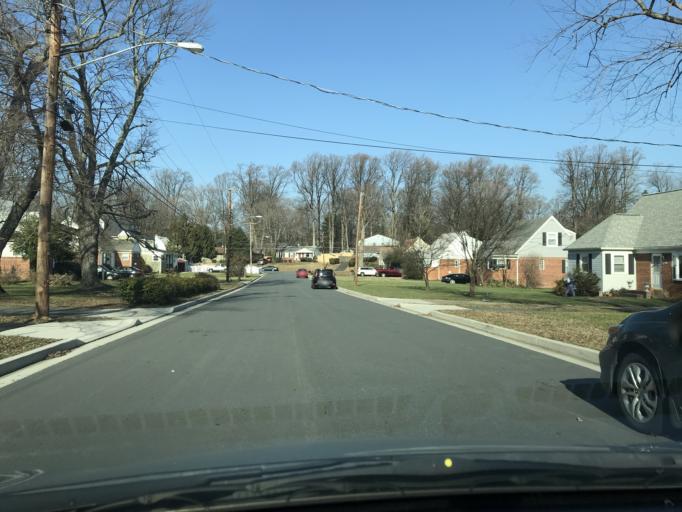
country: US
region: Virginia
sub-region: City of Fairfax
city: Fairfax
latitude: 38.8558
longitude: -77.3213
